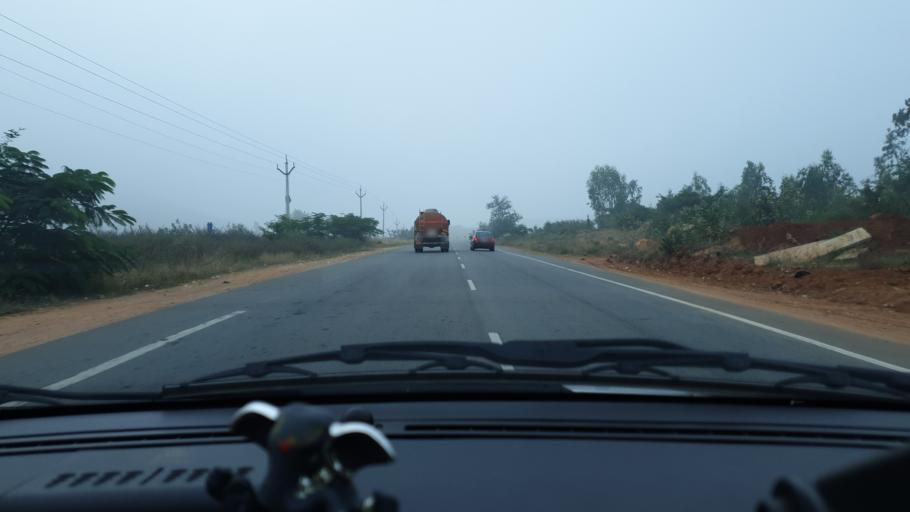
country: IN
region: Telangana
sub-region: Mahbubnagar
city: Farrukhnagar
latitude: 16.9160
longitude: 78.5271
